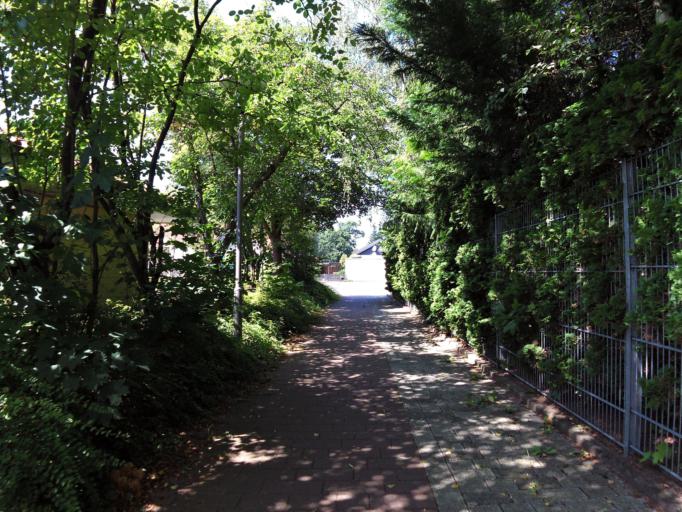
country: DE
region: Rheinland-Pfalz
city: Neuhemsbach
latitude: 49.4928
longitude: 7.9246
